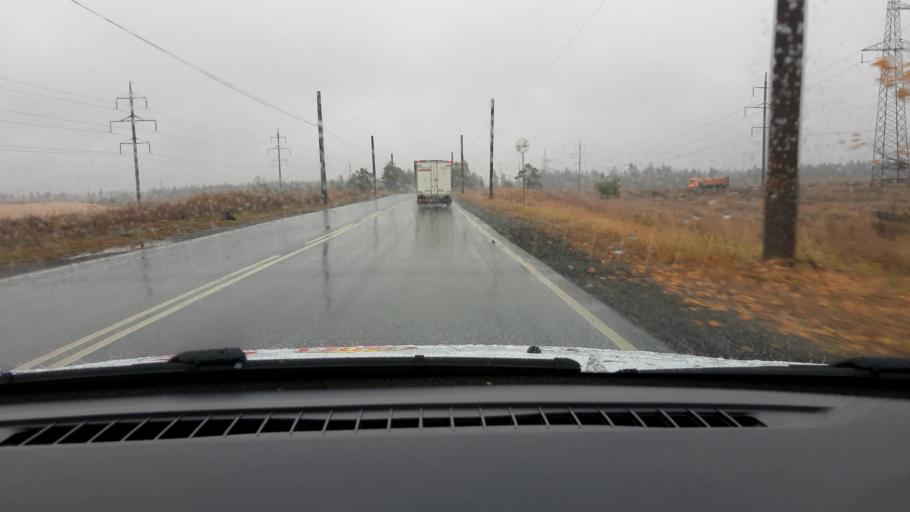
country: RU
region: Nizjnij Novgorod
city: Babino
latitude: 56.2779
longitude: 43.5629
